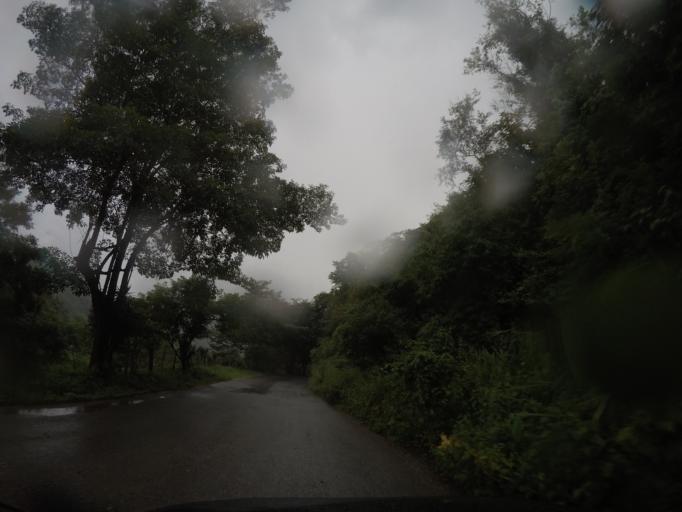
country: MX
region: Oaxaca
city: San Gabriel Mixtepec
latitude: 16.1084
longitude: -97.0657
